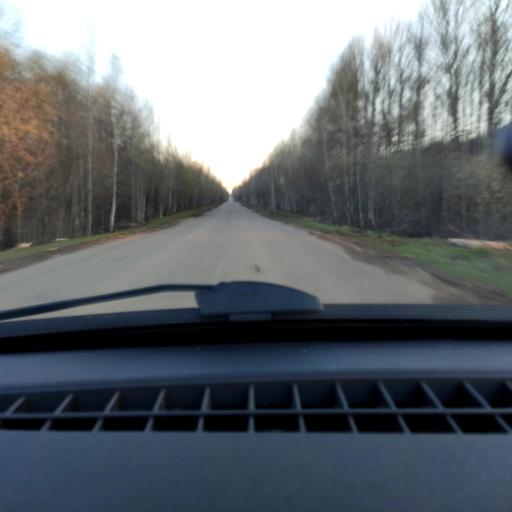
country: RU
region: Bashkortostan
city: Chishmy
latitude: 54.4383
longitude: 55.5610
